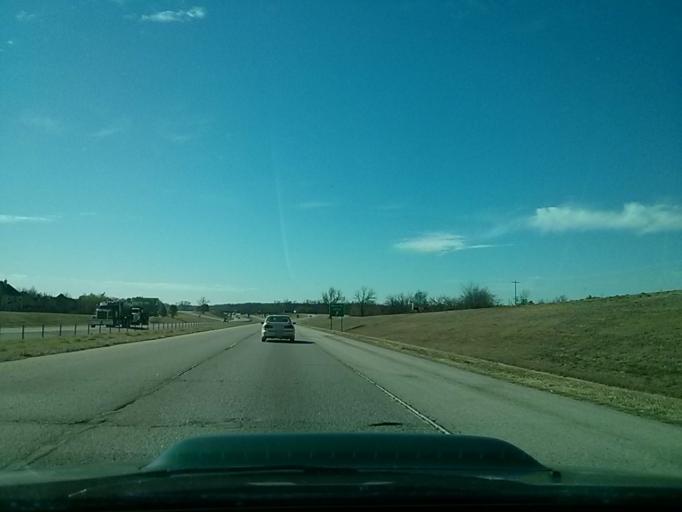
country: US
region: Oklahoma
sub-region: Tulsa County
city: Jenks
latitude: 36.0306
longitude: -96.0103
